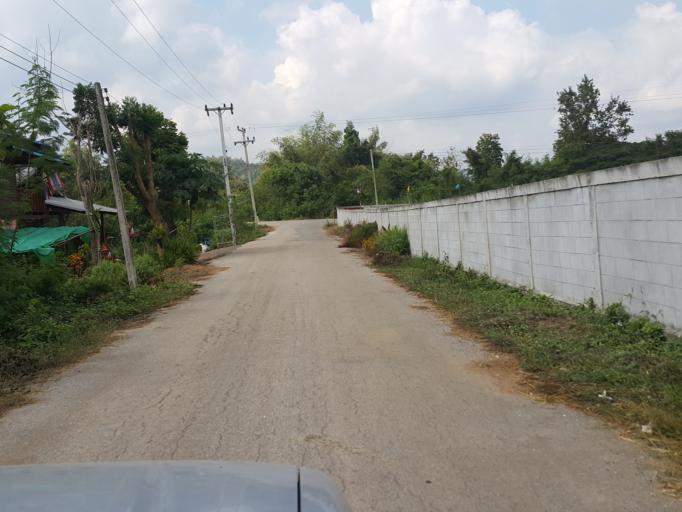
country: TH
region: Sukhothai
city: Thung Saliam
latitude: 17.4076
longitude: 99.5761
